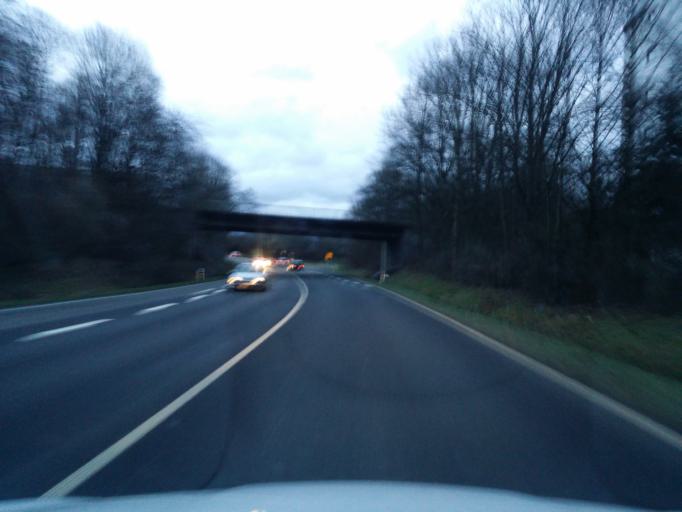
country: DE
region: Hesse
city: Liederbach
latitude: 50.1282
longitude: 8.4831
